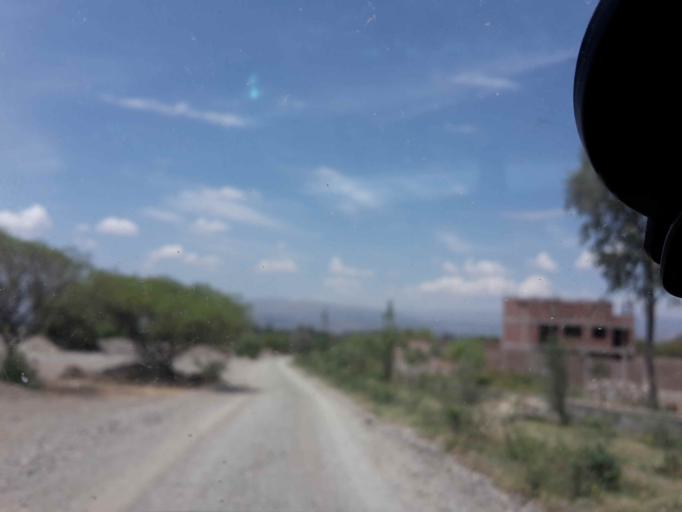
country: BO
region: Cochabamba
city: Cochabamba
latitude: -17.3320
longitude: -66.2125
